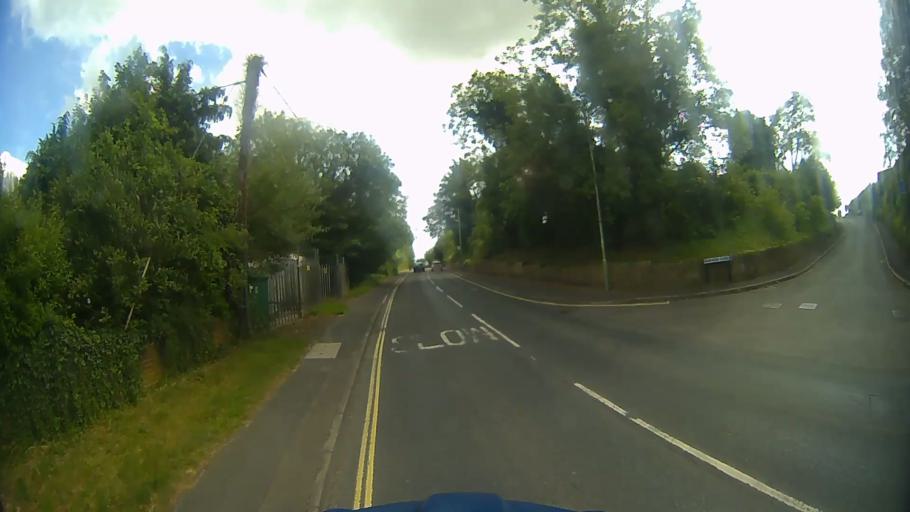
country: GB
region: England
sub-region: Hampshire
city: Andover
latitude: 51.2173
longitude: -1.4968
